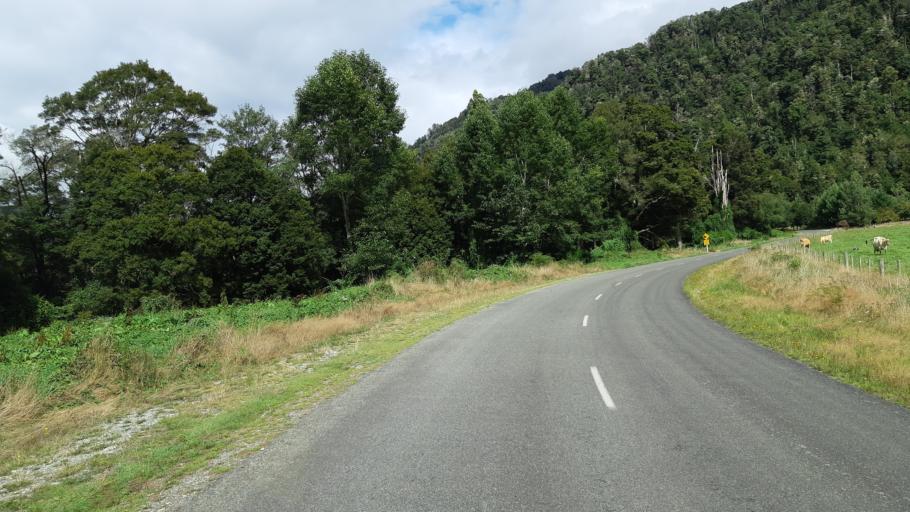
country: NZ
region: Tasman
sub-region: Tasman District
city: Wakefield
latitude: -41.7729
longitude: 172.3776
